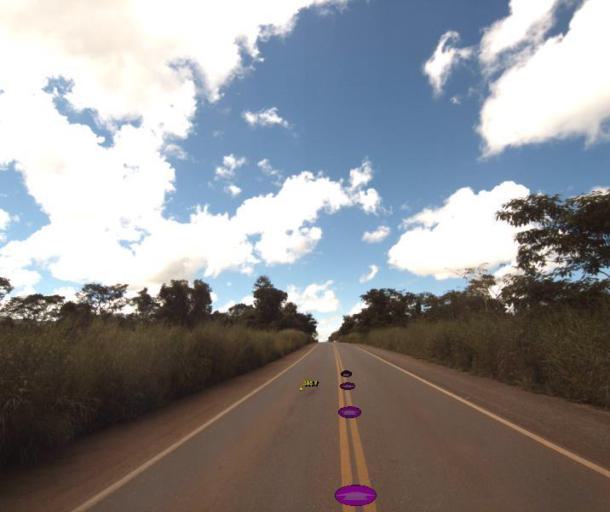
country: BR
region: Goias
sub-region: Petrolina De Goias
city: Petrolina de Goias
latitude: -16.0030
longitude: -49.1367
